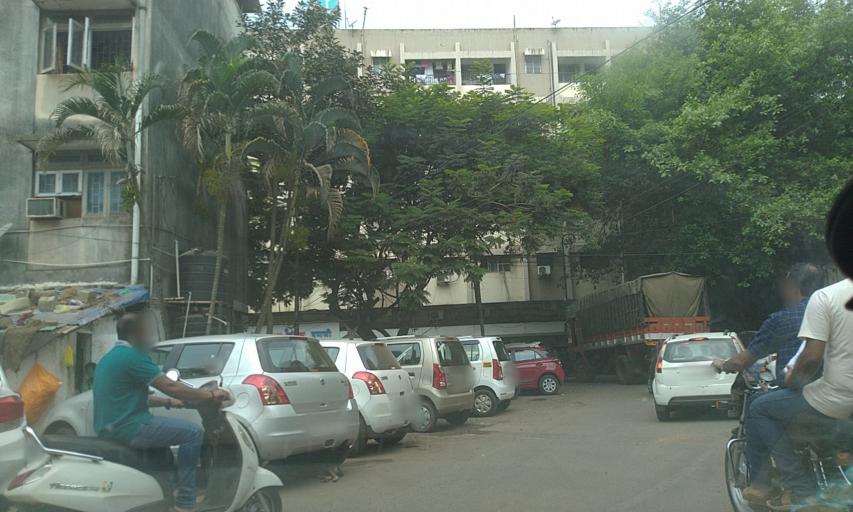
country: IN
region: Goa
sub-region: North Goa
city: Panaji
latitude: 15.4944
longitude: 73.8213
